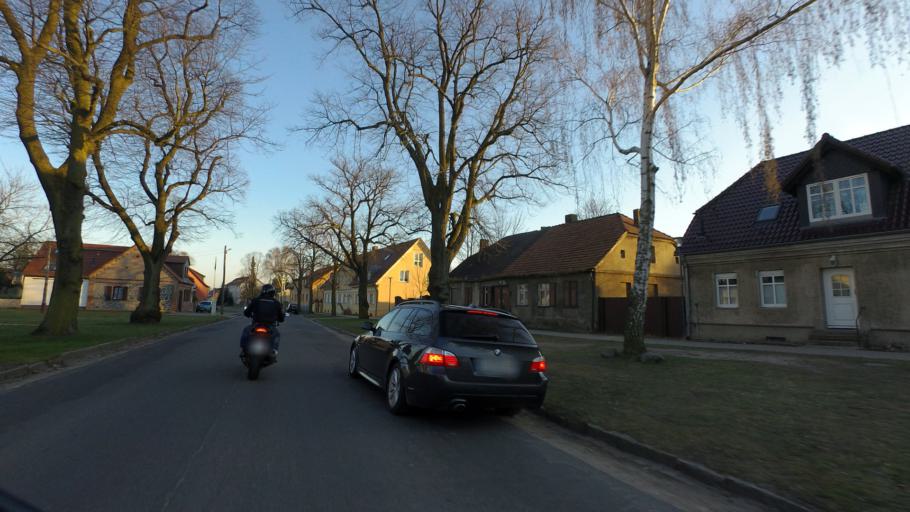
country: DE
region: Berlin
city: Hellersdorf
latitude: 52.5483
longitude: 13.6366
